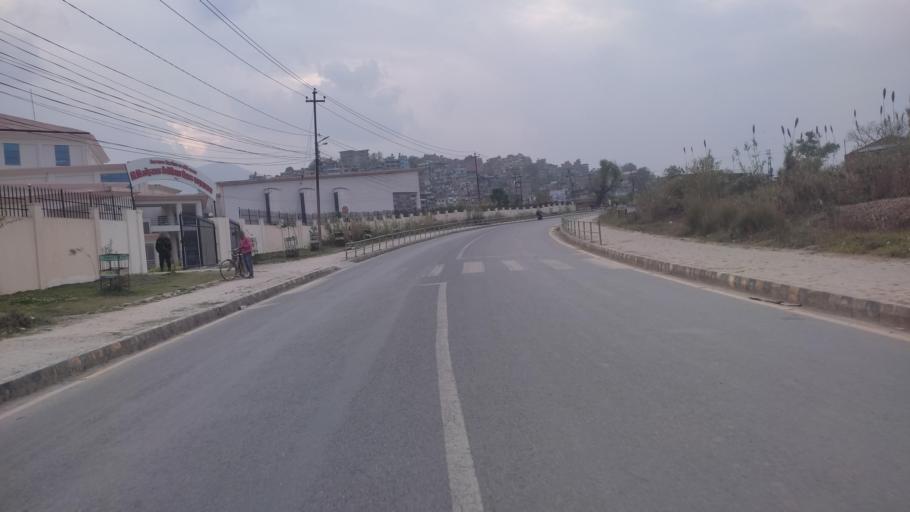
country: NP
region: Central Region
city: Kirtipur
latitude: 27.6759
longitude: 85.2852
